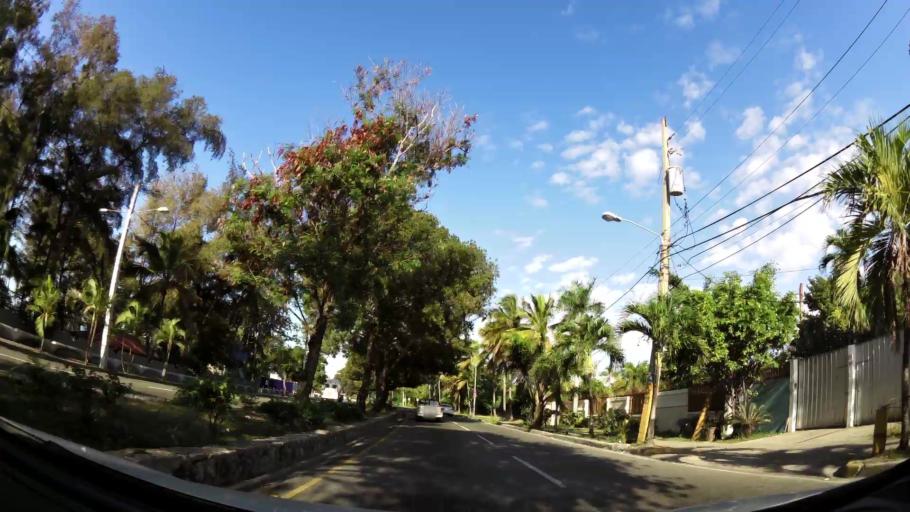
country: DO
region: Santo Domingo
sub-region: Santo Domingo
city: Santo Domingo Este
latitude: 18.4689
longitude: -69.8495
